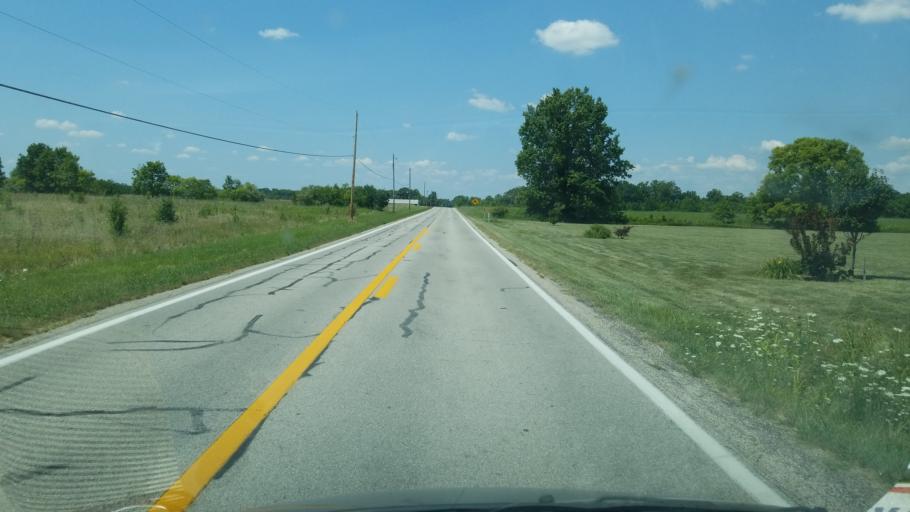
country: US
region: Ohio
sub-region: Franklin County
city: Lake Darby
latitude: 39.9850
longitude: -83.2312
